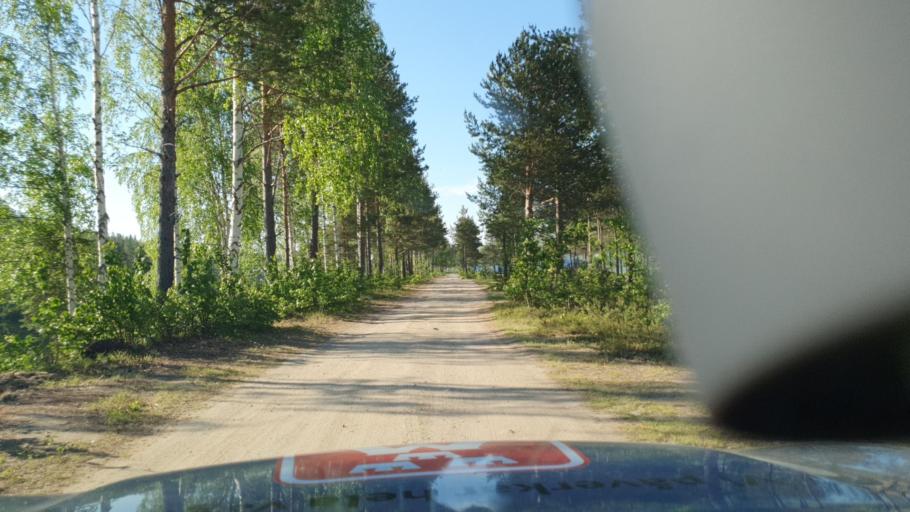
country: SE
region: Norrbotten
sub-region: Alvsbyns Kommun
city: AElvsbyn
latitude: 66.2195
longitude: 20.8600
